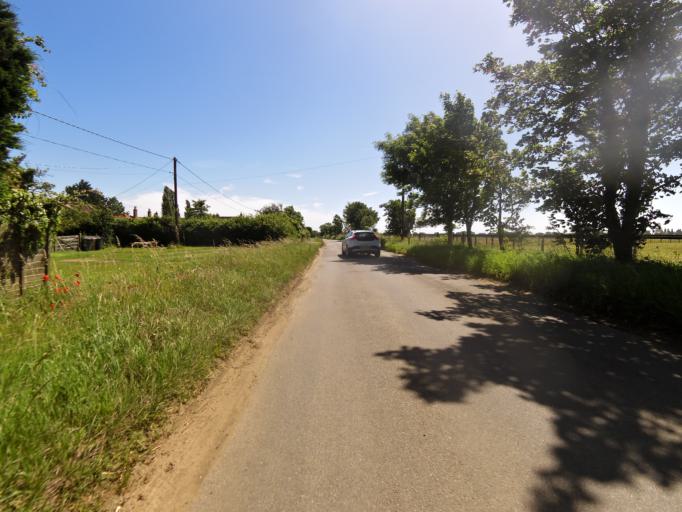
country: GB
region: England
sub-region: Suffolk
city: Wickham Market
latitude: 52.0585
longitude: 1.4403
